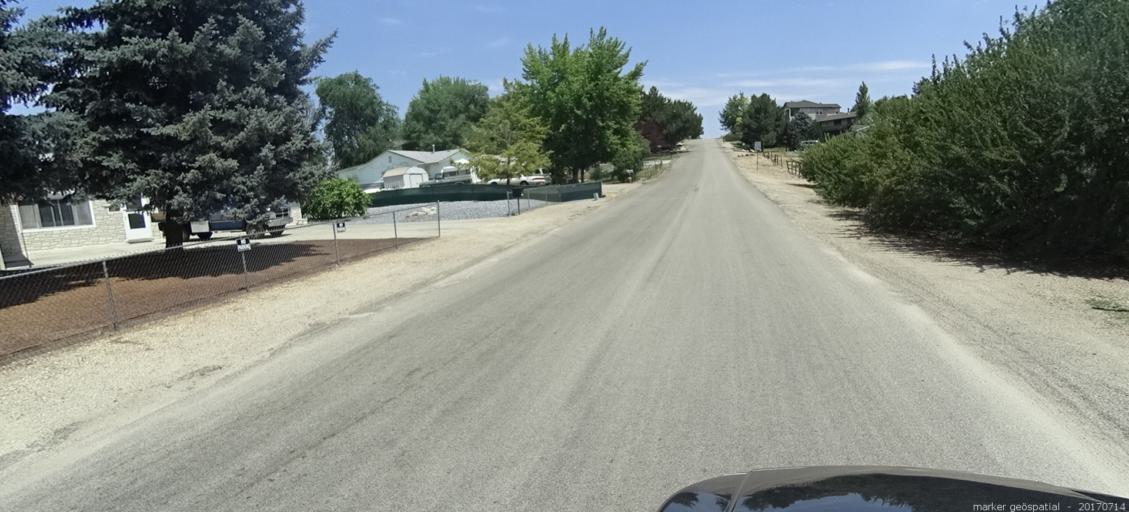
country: US
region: Idaho
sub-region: Ada County
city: Meridian
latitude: 43.5392
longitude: -116.3342
